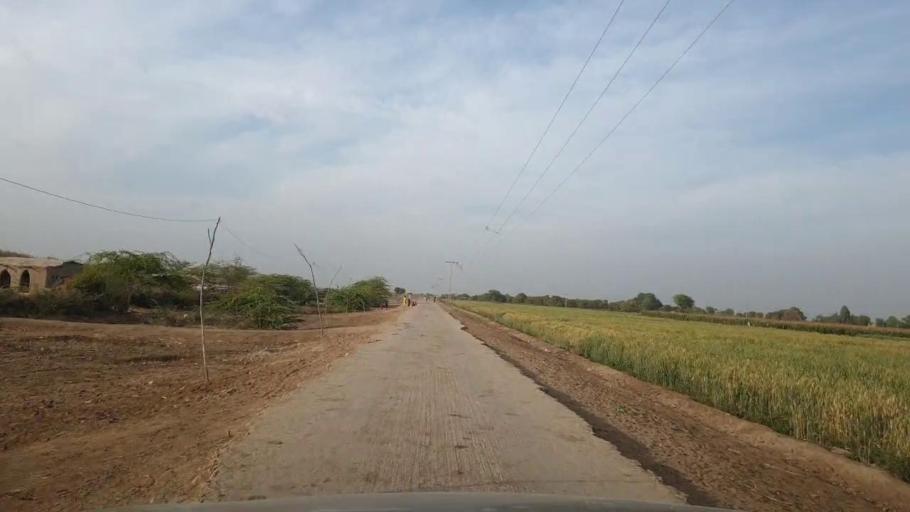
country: PK
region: Sindh
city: Kunri
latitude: 25.1977
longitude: 69.5199
